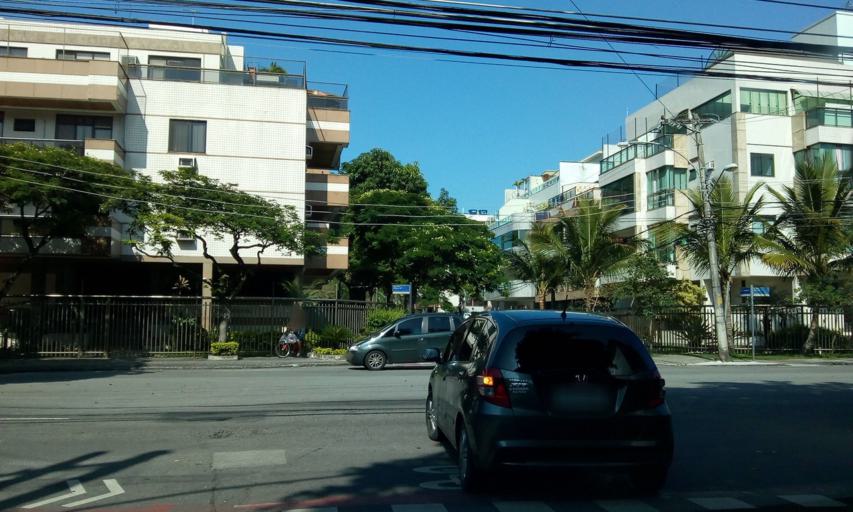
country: BR
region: Rio de Janeiro
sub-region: Nilopolis
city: Nilopolis
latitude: -23.0195
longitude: -43.4589
